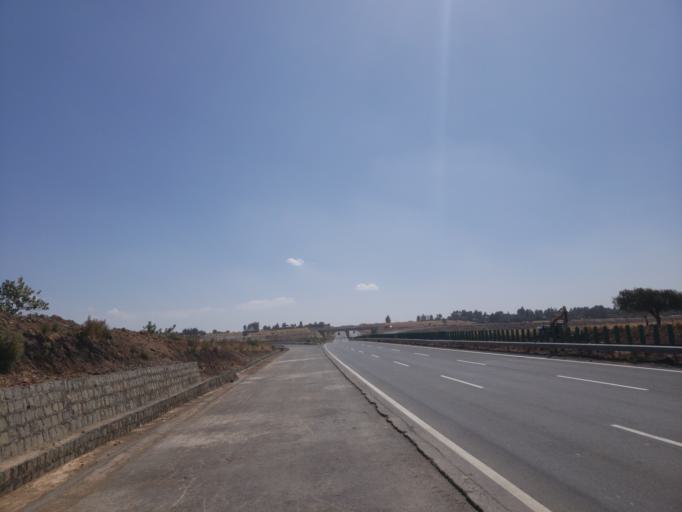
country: ET
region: Oromiya
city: Mojo
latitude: 8.5826
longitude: 39.1694
